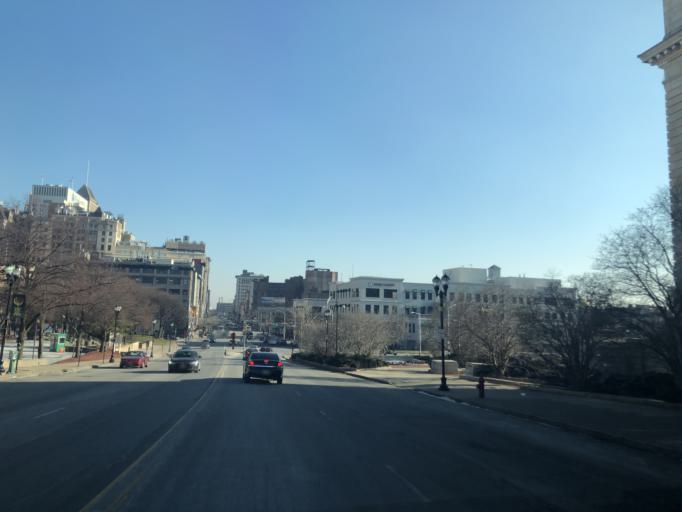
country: US
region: New Jersey
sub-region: Essex County
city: Newark
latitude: 40.7376
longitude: -74.1788
